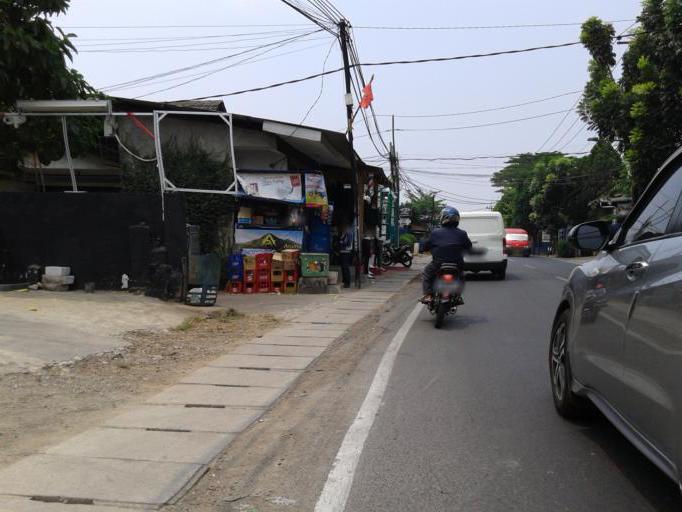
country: ID
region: Banten
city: South Tangerang
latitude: -6.2799
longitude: 106.7619
